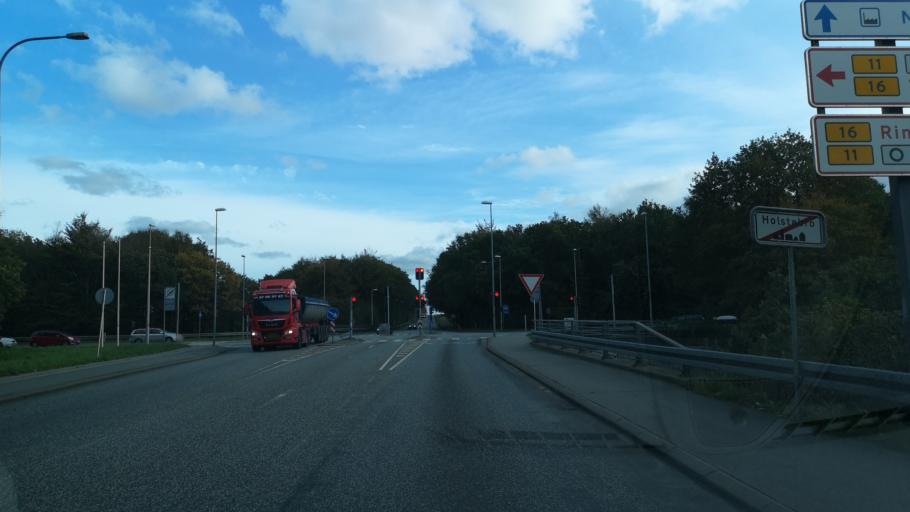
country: DK
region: Central Jutland
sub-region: Holstebro Kommune
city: Holstebro
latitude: 56.3462
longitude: 8.6307
